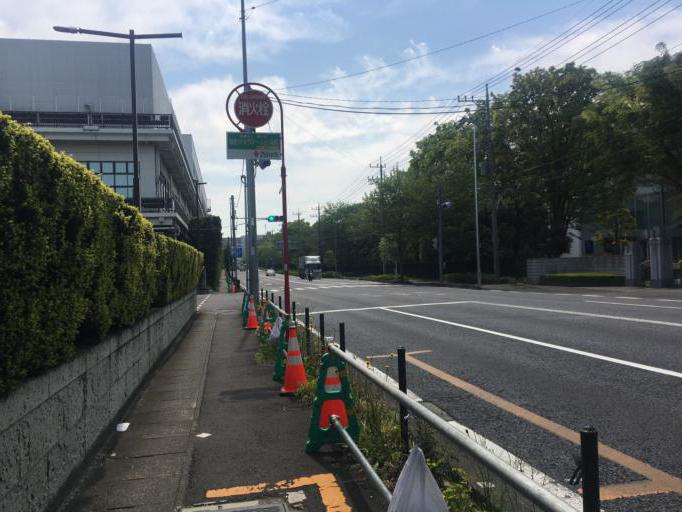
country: JP
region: Saitama
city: Wako
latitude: 35.7811
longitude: 139.6144
